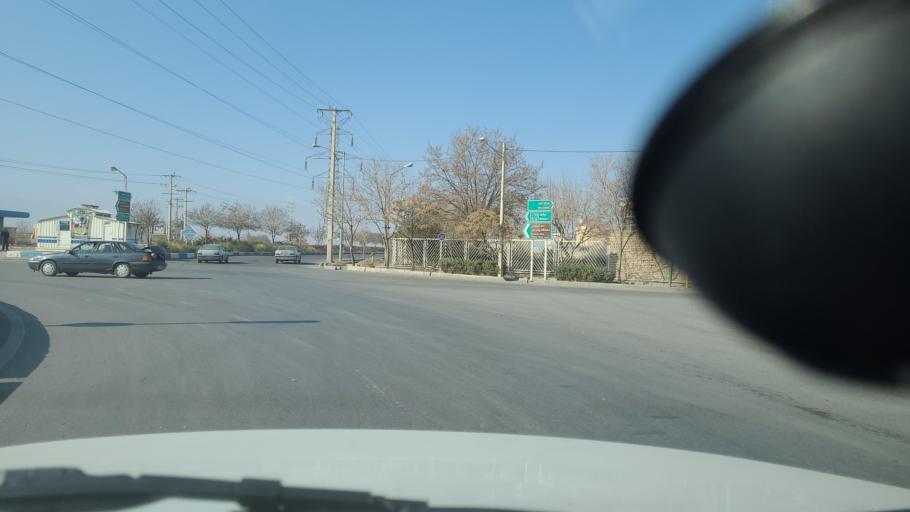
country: IR
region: Razavi Khorasan
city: Fariman
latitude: 35.6949
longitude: 59.8445
